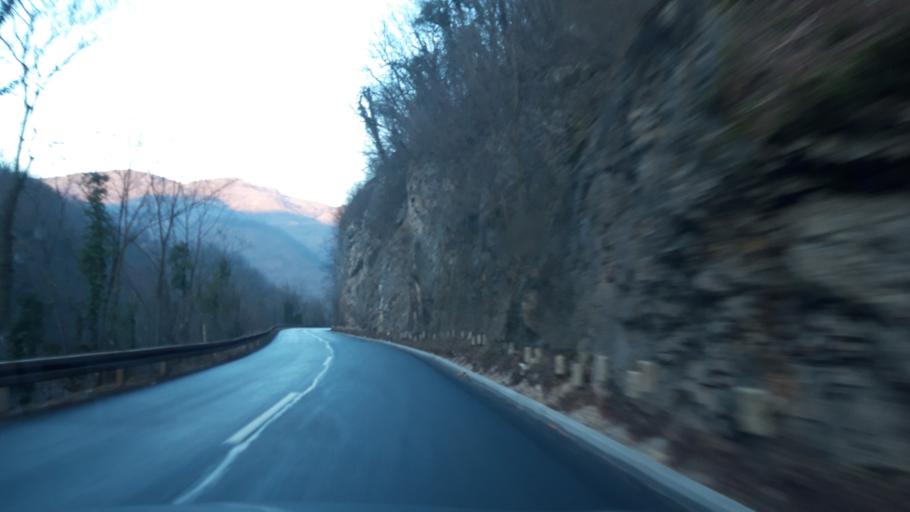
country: BA
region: Republika Srpska
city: Milici
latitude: 44.2703
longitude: 19.1051
